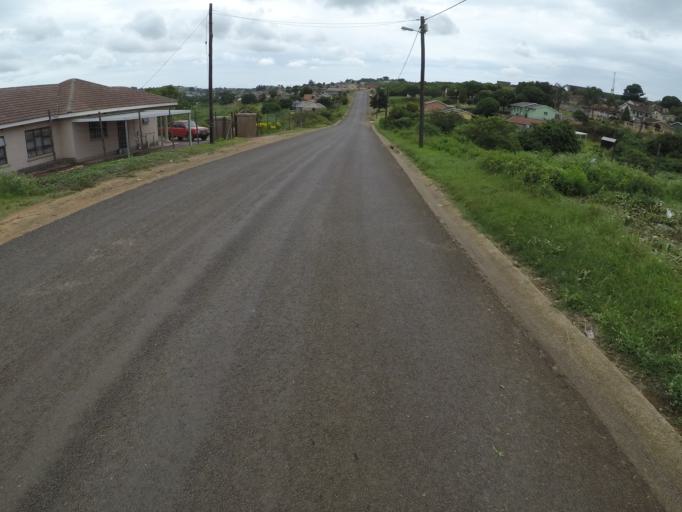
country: ZA
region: KwaZulu-Natal
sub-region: uThungulu District Municipality
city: Empangeni
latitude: -28.7784
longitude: 31.8574
